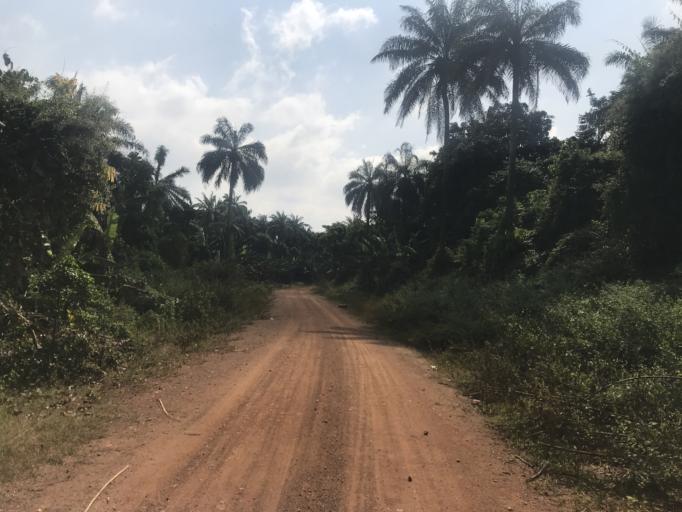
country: NG
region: Osun
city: Ibokun
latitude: 7.8163
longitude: 4.6454
